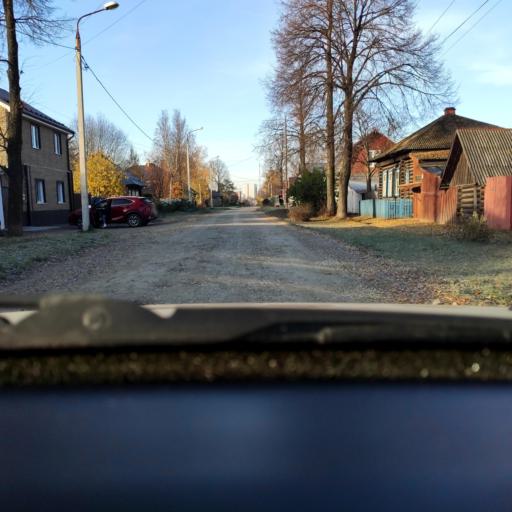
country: RU
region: Perm
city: Perm
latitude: 58.0249
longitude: 56.3303
